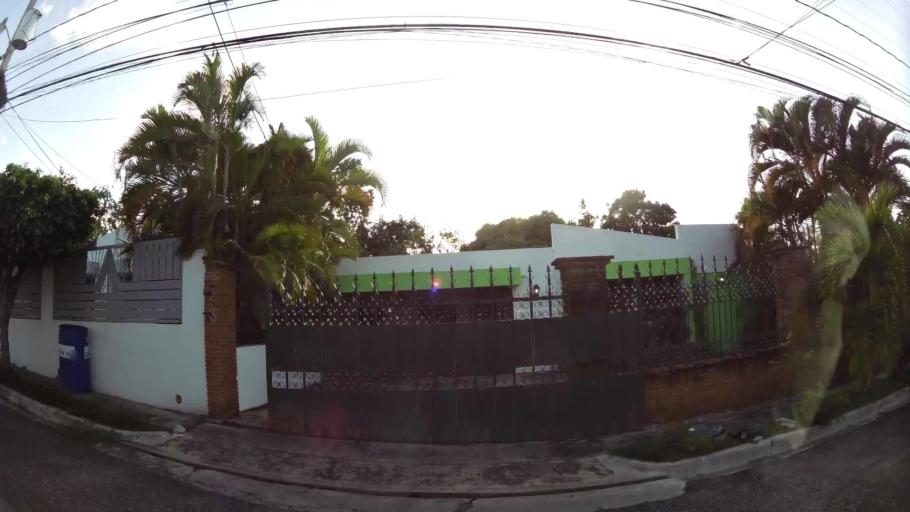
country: DO
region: Nacional
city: Santo Domingo
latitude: 18.4953
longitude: -69.9696
